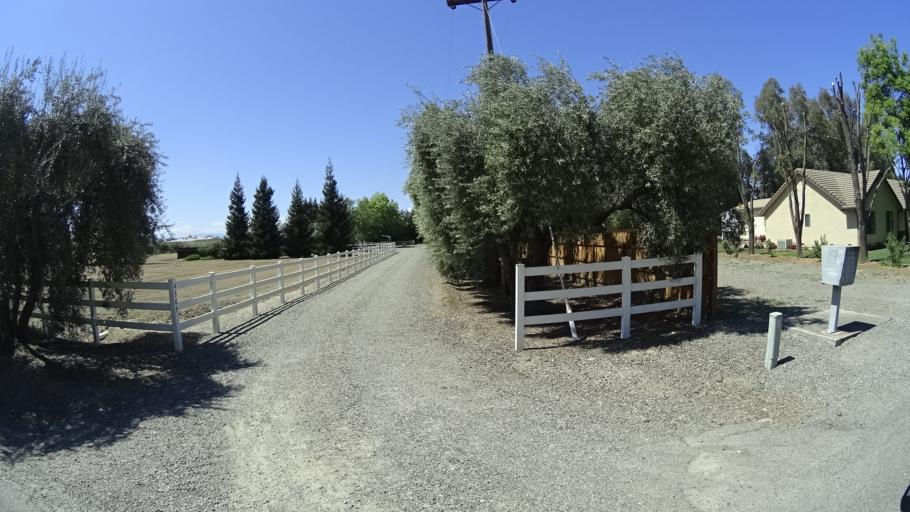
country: US
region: California
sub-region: Glenn County
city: Orland
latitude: 39.7382
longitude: -122.1898
